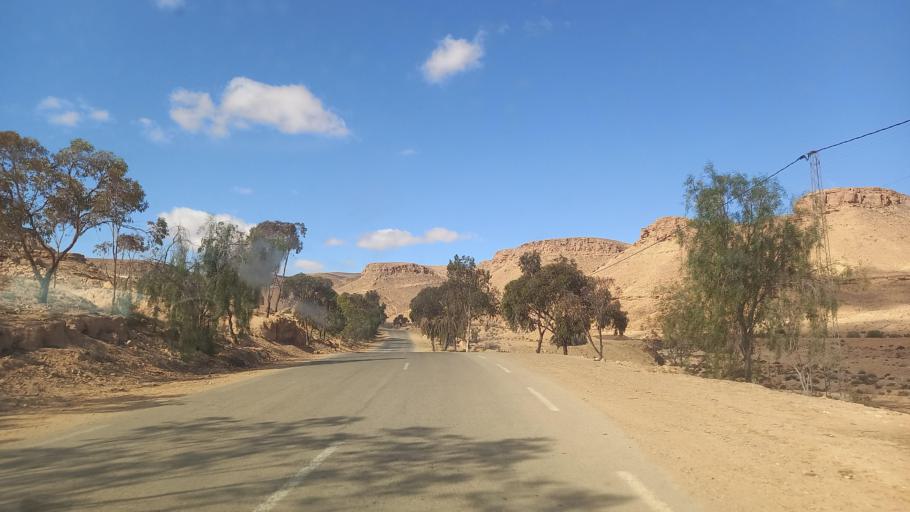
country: TN
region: Tataouine
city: Tataouine
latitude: 32.9173
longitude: 10.2691
